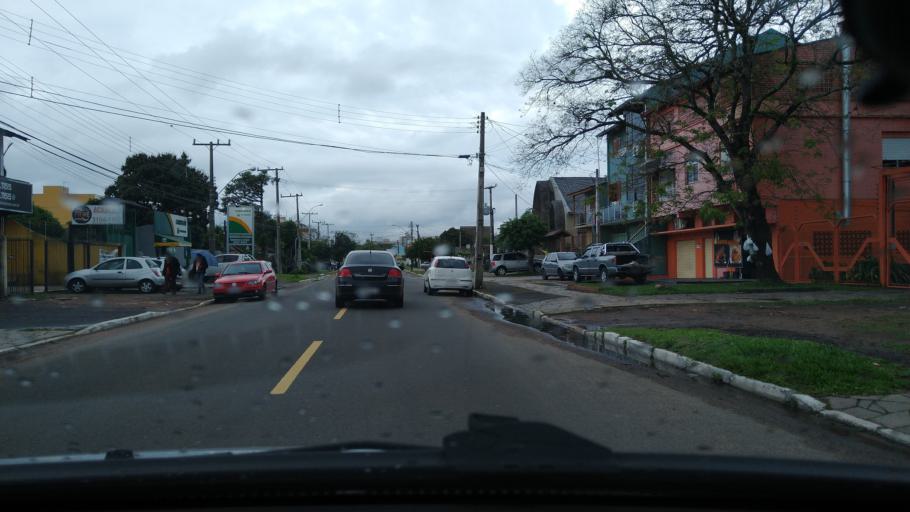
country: BR
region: Rio Grande do Sul
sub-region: Canoas
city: Canoas
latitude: -29.9184
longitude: -51.1940
